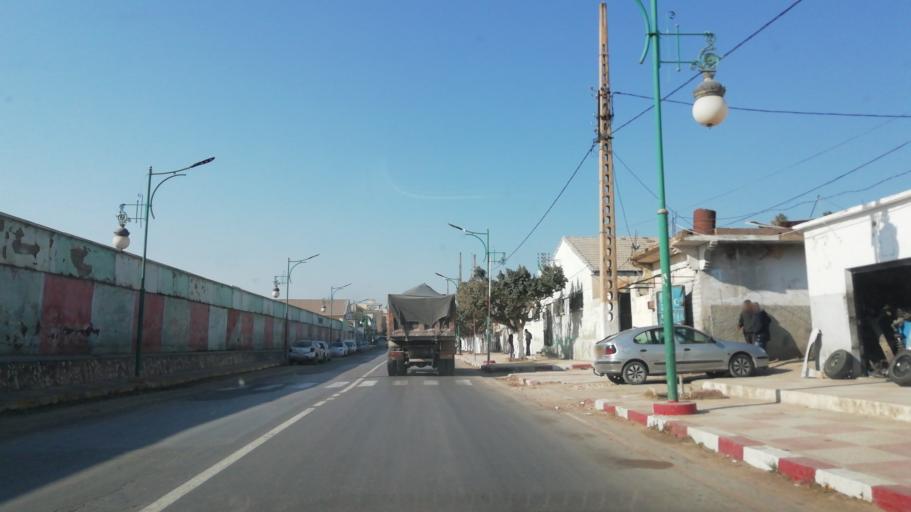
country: DZ
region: Relizane
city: Relizane
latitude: 35.7341
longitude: 0.4639
